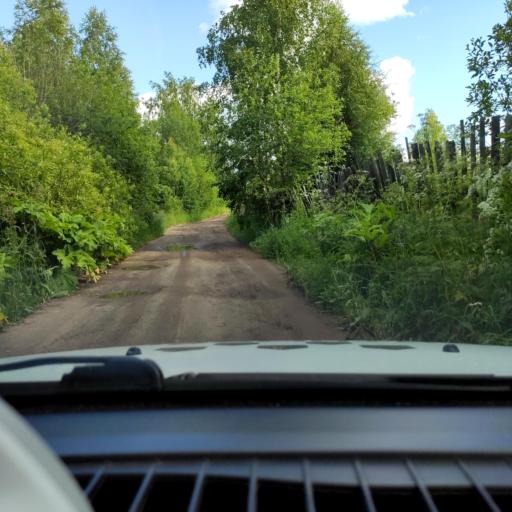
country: RU
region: Perm
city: Overyata
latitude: 58.1042
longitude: 55.8678
